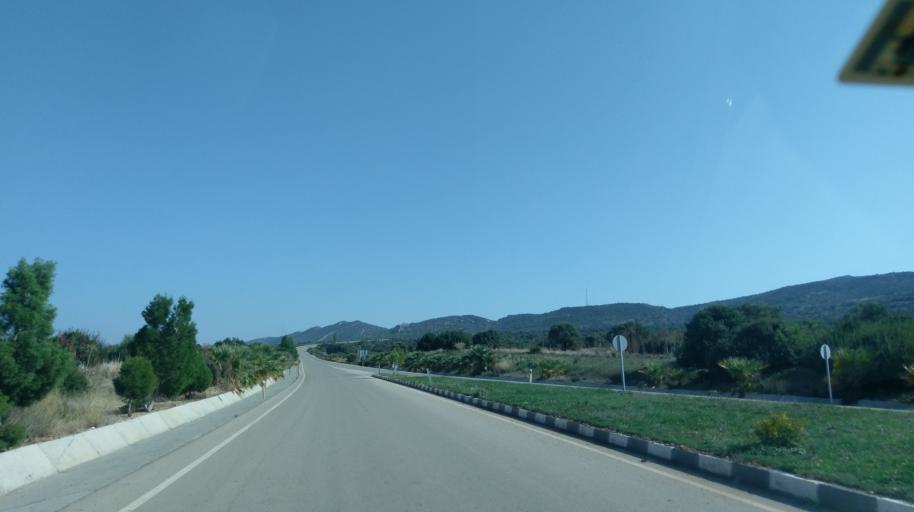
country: CY
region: Ammochostos
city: Trikomo
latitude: 35.4376
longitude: 33.9517
